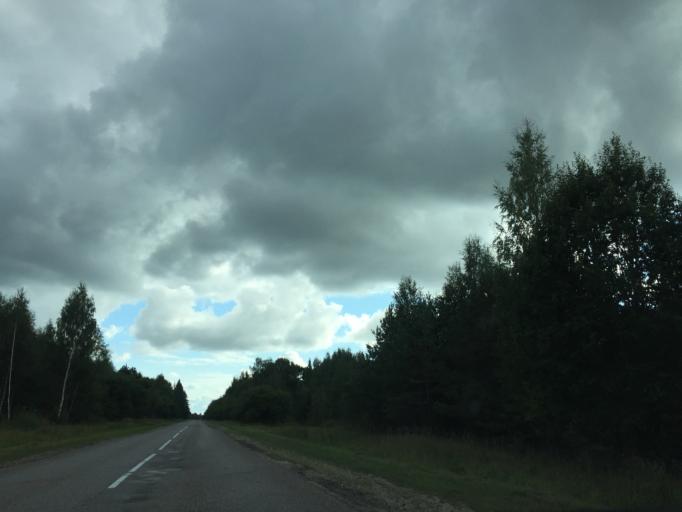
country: LV
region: Limbazu Rajons
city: Limbazi
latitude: 57.3645
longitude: 24.6714
